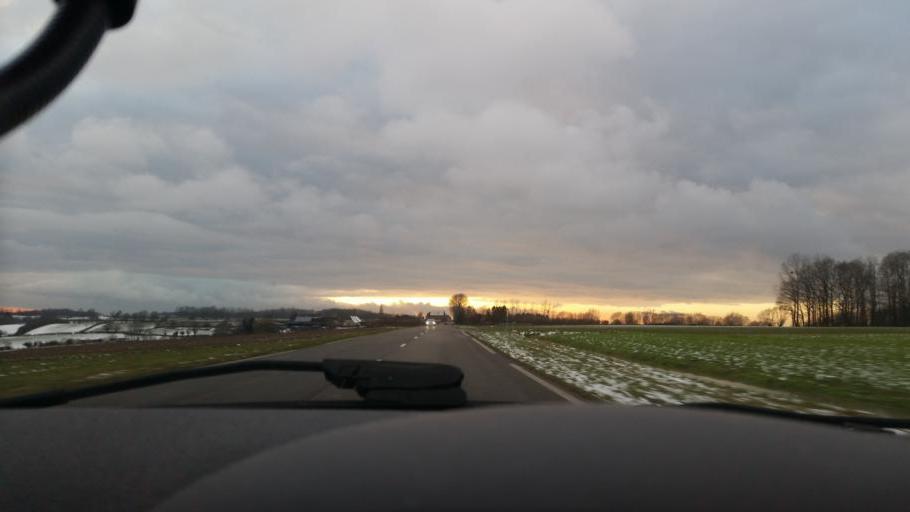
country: FR
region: Nord-Pas-de-Calais
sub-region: Departement du Nord
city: Jeumont
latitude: 50.2507
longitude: 4.1141
